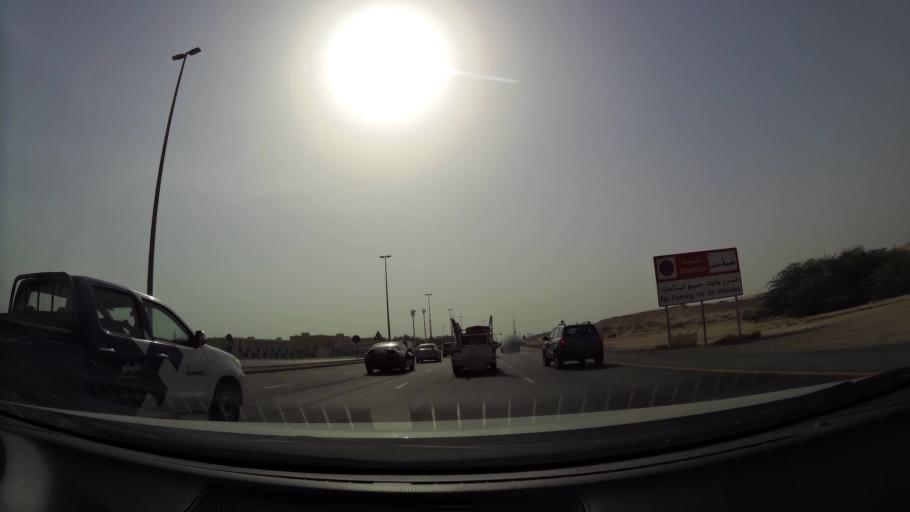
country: AE
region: Ash Shariqah
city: Sharjah
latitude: 25.2708
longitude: 55.4414
